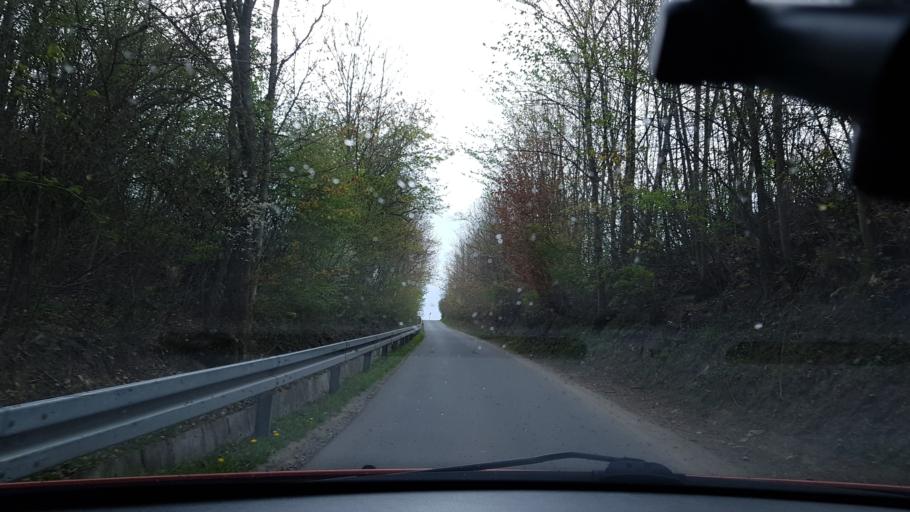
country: PL
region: Lower Silesian Voivodeship
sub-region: Powiat klodzki
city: Bystrzyca Klodzka
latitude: 50.3072
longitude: 16.6132
